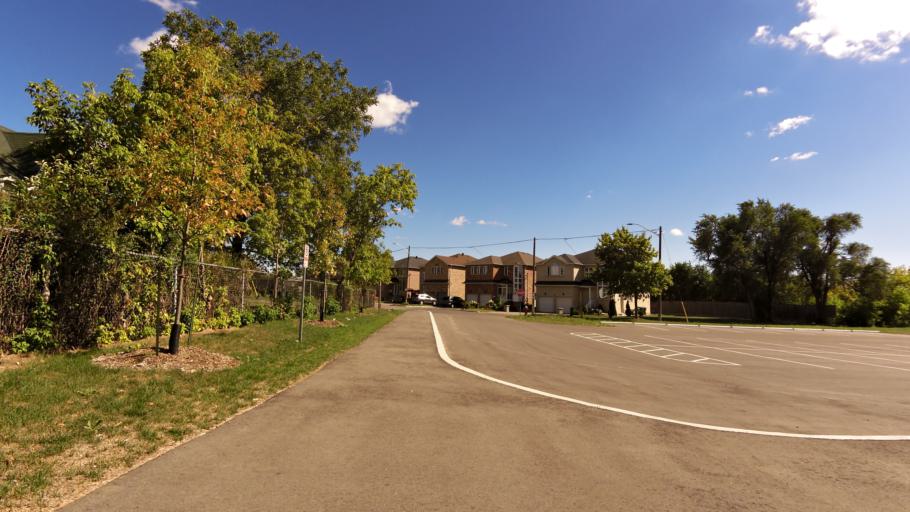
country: CA
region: Ontario
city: Etobicoke
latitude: 43.7058
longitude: -79.6503
